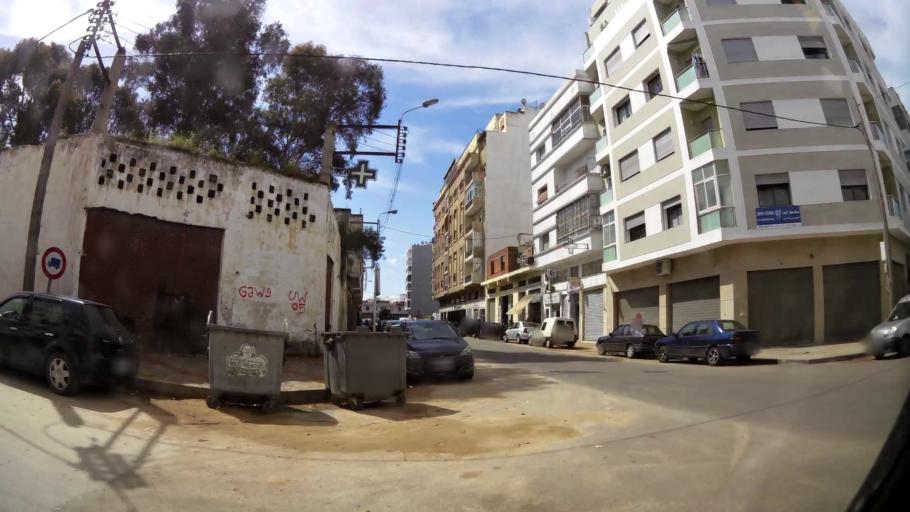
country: MA
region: Grand Casablanca
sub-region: Casablanca
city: Casablanca
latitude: 33.5919
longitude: -7.5984
